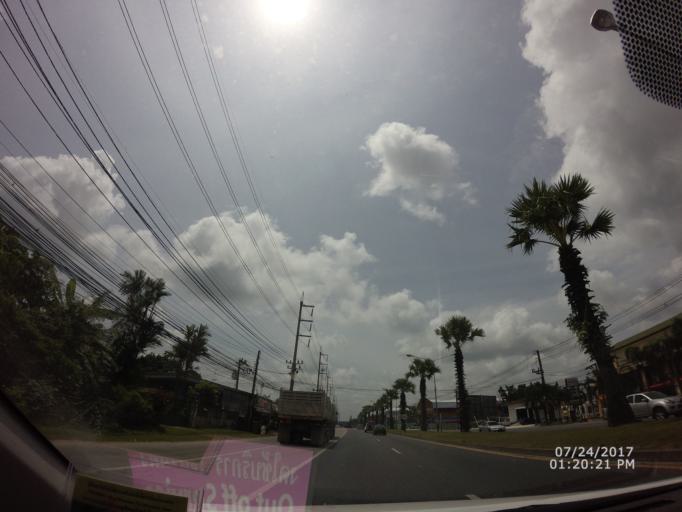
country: TH
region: Phuket
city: Thalang
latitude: 8.0689
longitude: 98.3428
